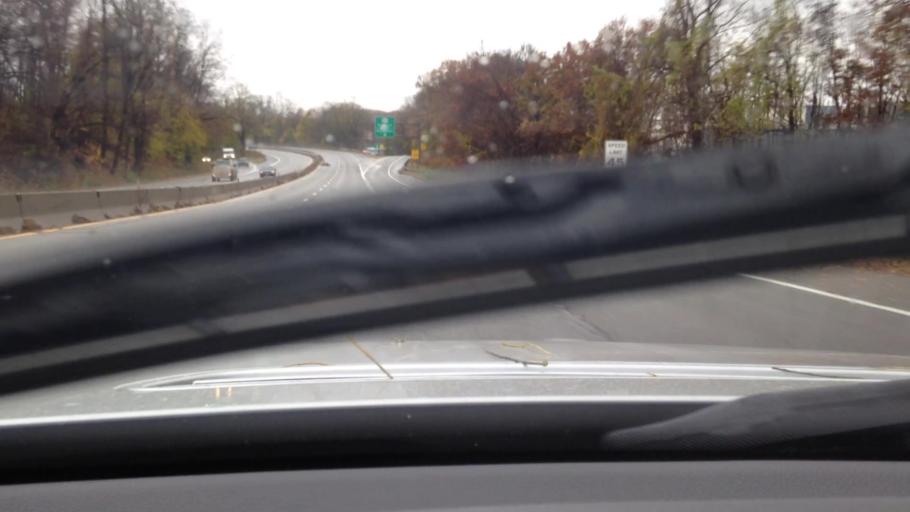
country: US
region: New York
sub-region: Westchester County
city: Buchanan
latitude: 41.2739
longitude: -73.9326
